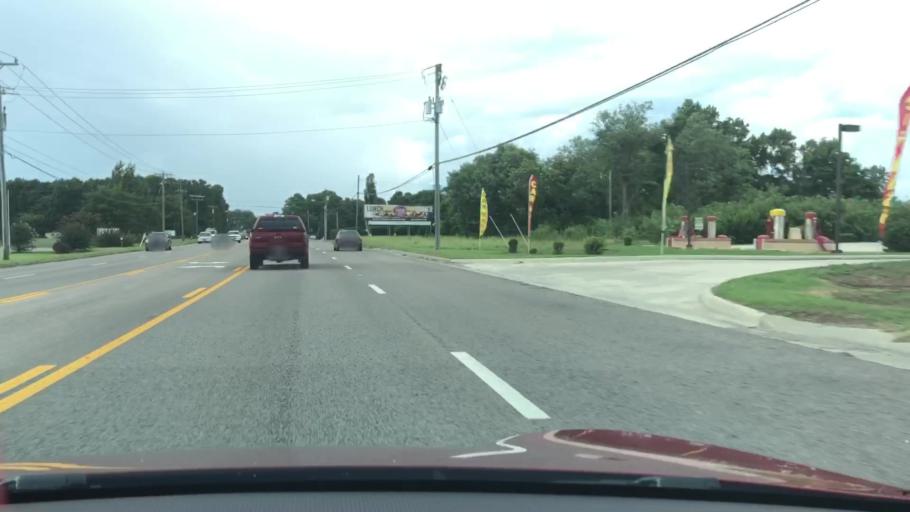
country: US
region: North Carolina
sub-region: Dare County
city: Southern Shores
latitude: 36.2341
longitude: -75.8740
